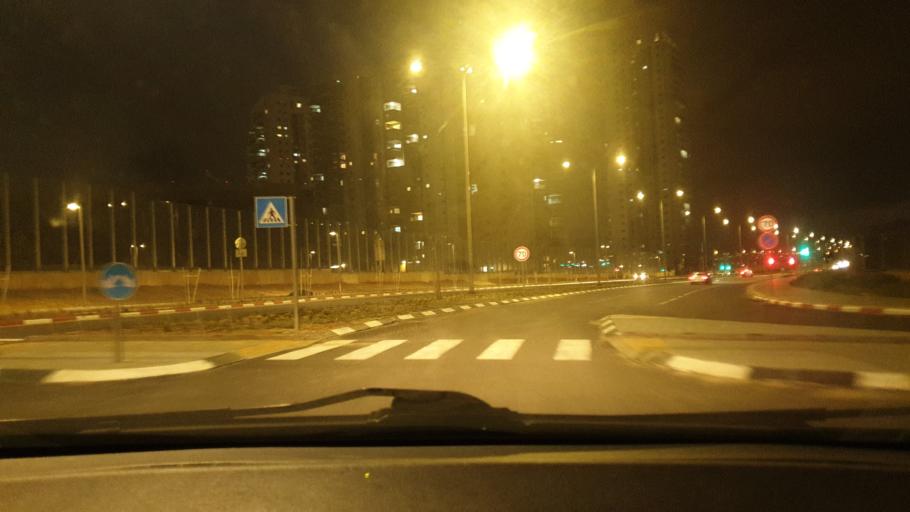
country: IL
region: Central District
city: Ramla
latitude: 31.9355
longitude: 34.8513
